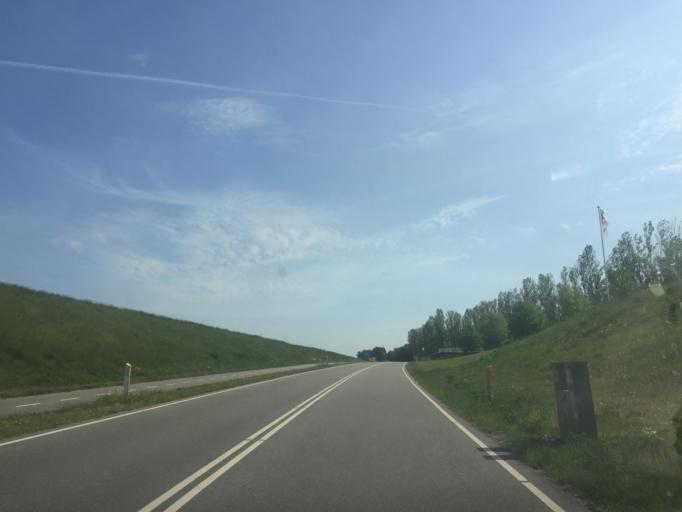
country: DK
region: Capital Region
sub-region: Egedal Kommune
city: Smorumnedre
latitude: 55.7177
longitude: 12.2960
